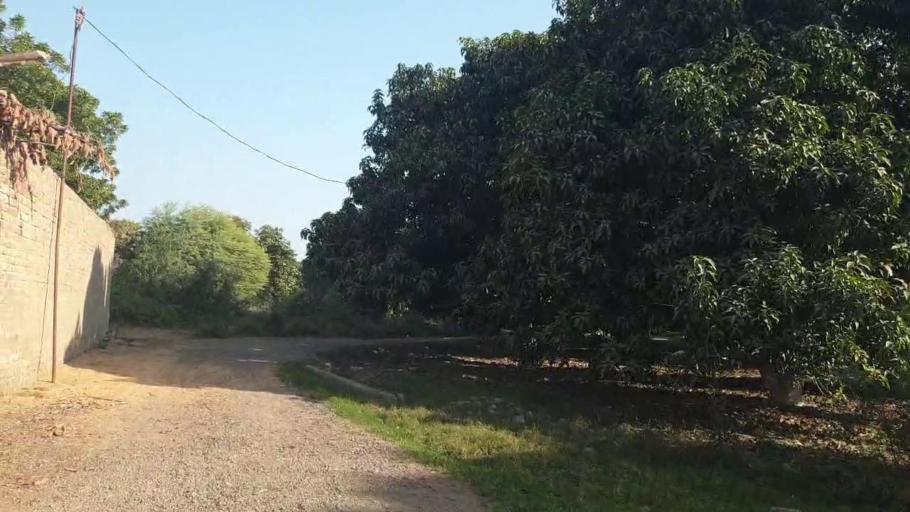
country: PK
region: Sindh
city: Matiari
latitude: 25.5307
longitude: 68.4353
